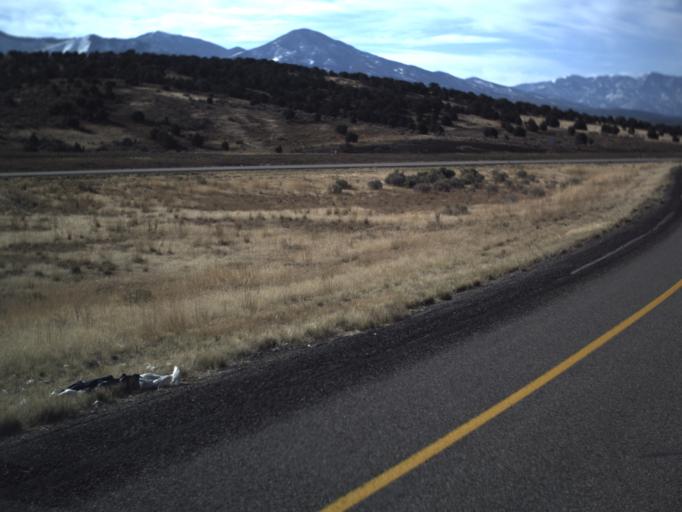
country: US
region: Utah
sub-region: Millard County
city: Fillmore
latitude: 39.1434
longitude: -112.2379
